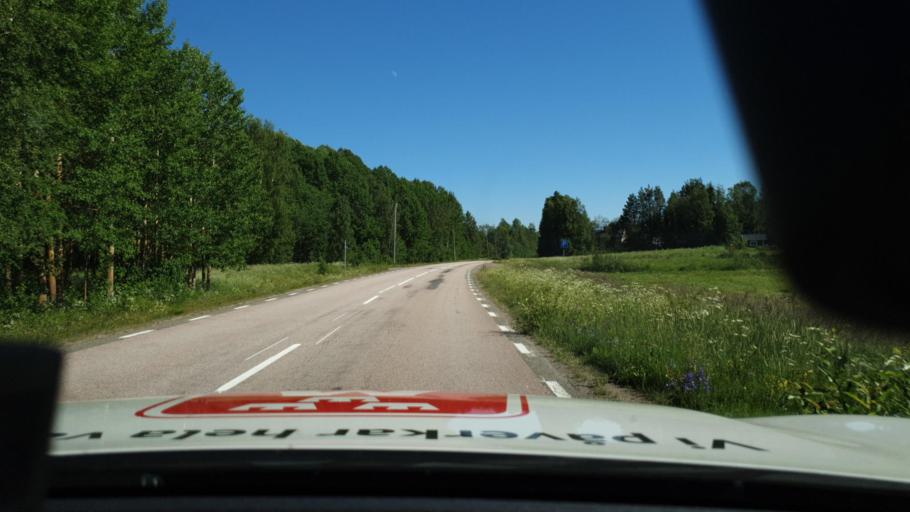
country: SE
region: Norrbotten
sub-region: Lulea Kommun
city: Ranea
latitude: 65.9267
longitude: 22.4336
